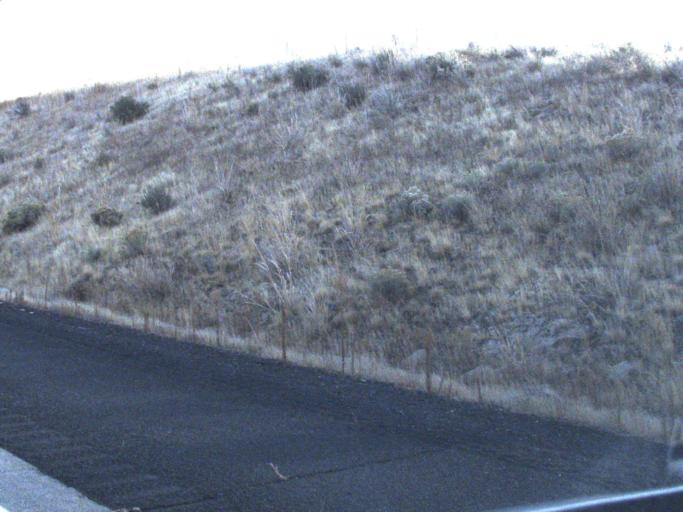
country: US
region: Washington
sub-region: Franklin County
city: Connell
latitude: 46.8822
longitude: -118.6203
